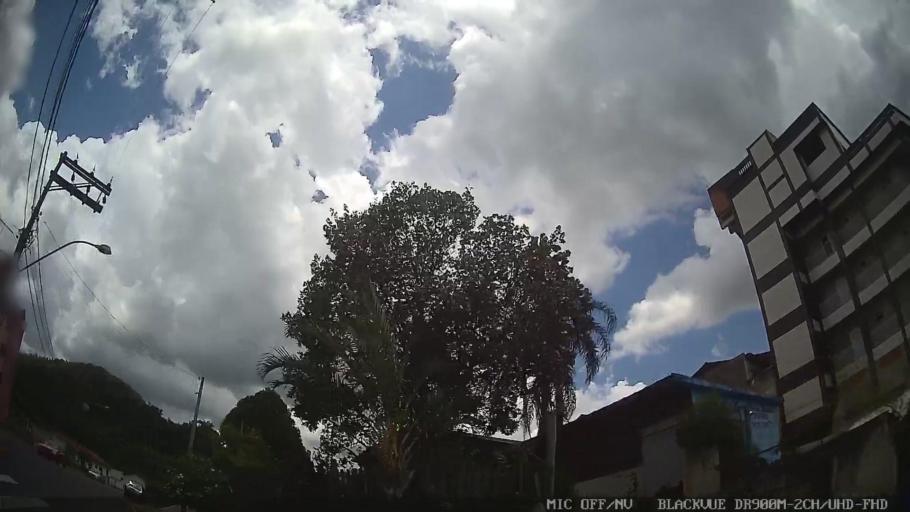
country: BR
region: Sao Paulo
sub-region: Serra Negra
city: Serra Negra
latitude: -22.5941
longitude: -46.7055
